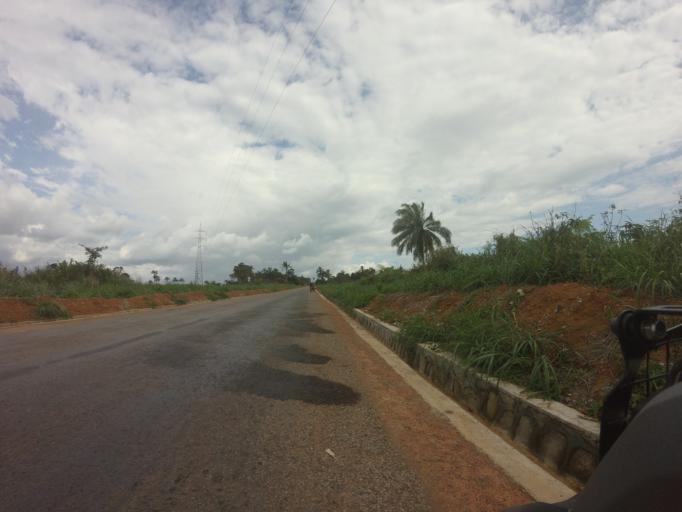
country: CD
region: Bas-Congo
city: Matadi
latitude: -5.4876
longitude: 13.3430
